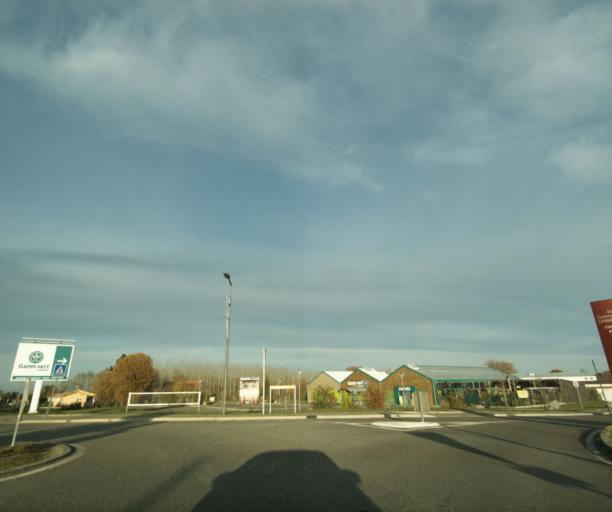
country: FR
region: Aquitaine
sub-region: Departement des Landes
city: Gabarret
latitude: 43.9776
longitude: 0.0071
